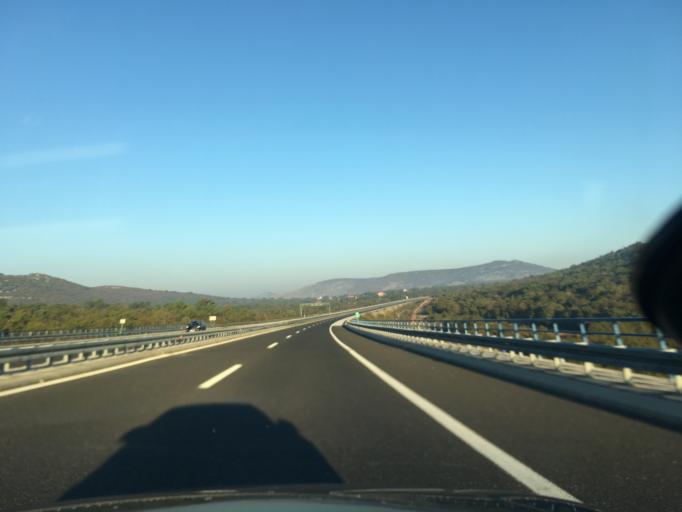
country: HR
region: Splitsko-Dalmatinska
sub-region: Grad Trogir
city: Trogir
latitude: 43.6330
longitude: 16.2213
